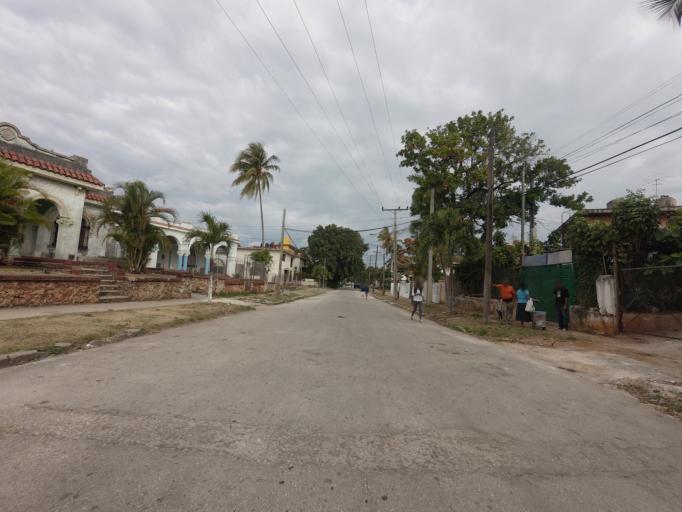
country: CU
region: La Habana
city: Havana
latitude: 23.1183
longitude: -82.4195
